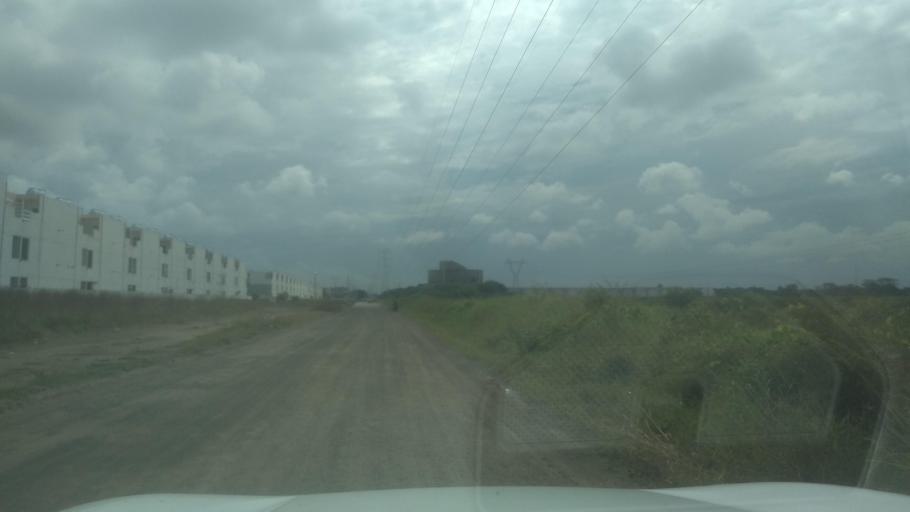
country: MX
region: Veracruz
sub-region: Medellin
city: Fraccionamiento Arboledas San Ramon
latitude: 19.0937
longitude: -96.1705
